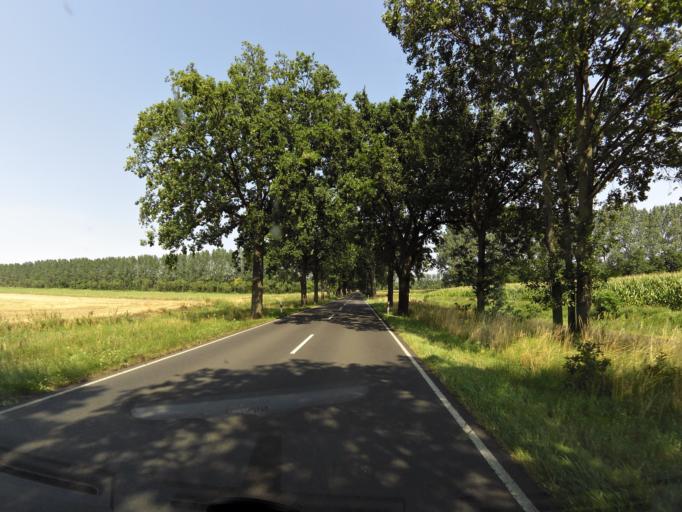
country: DE
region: Brandenburg
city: Liebenwalde
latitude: 52.8665
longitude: 13.3333
